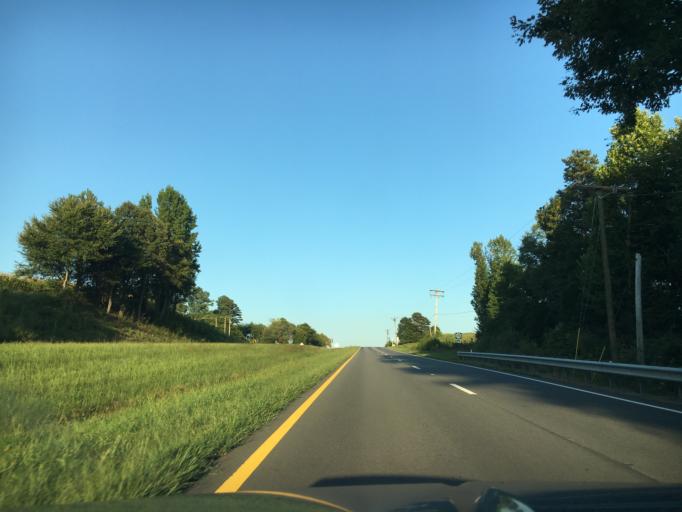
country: US
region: Virginia
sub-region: City of Danville
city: Danville
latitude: 36.5810
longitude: -79.1958
